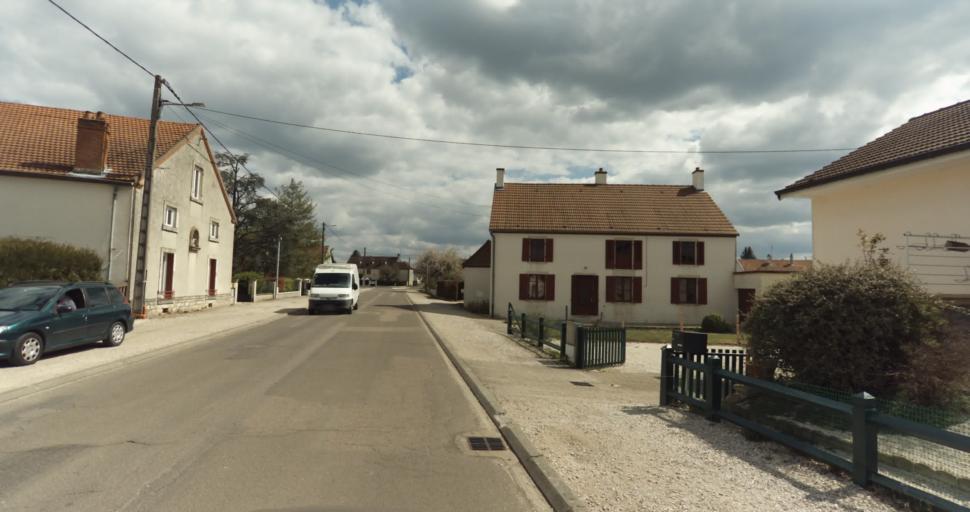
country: FR
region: Bourgogne
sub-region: Departement de la Cote-d'Or
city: Auxonne
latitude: 47.1848
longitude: 5.3948
